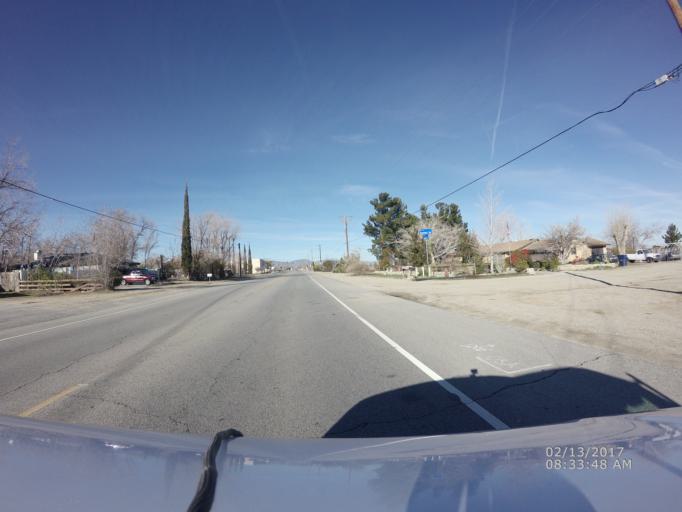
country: US
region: California
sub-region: Los Angeles County
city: Littlerock
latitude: 34.5430
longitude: -117.9725
